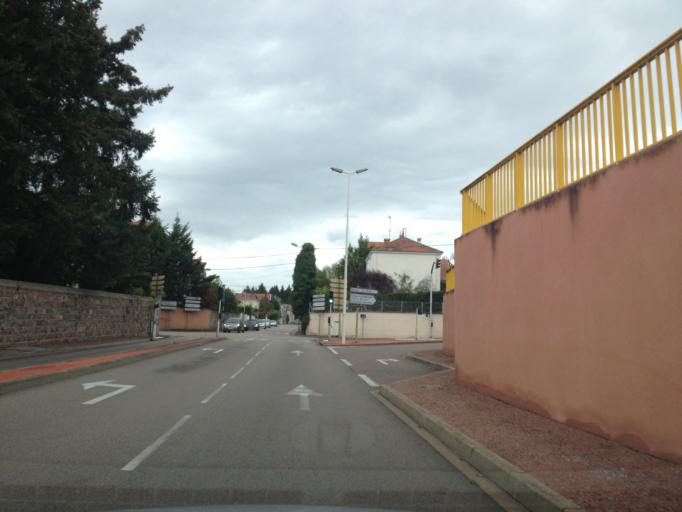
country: FR
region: Rhone-Alpes
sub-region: Departement de la Loire
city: Riorges
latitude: 46.0396
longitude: 4.0454
